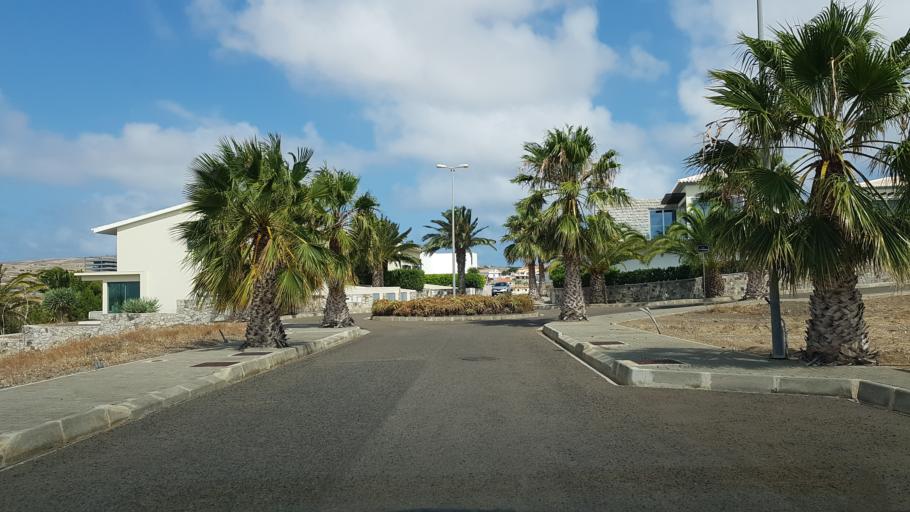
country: PT
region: Madeira
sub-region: Porto Santo
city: Vila de Porto Santo
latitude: 33.0678
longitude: -16.3346
